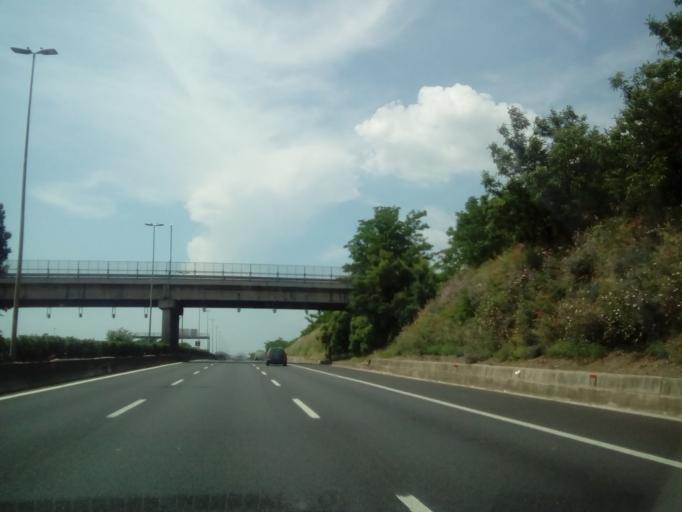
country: IT
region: Latium
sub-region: Citta metropolitana di Roma Capitale
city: Colle Verde
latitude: 41.9625
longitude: 12.5721
